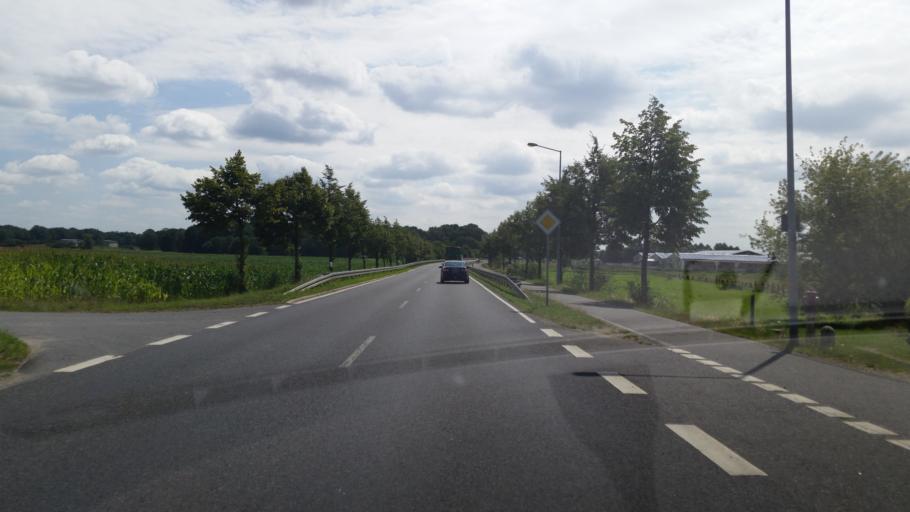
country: DE
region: Saxony
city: Kamenz
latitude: 51.2883
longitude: 14.1223
